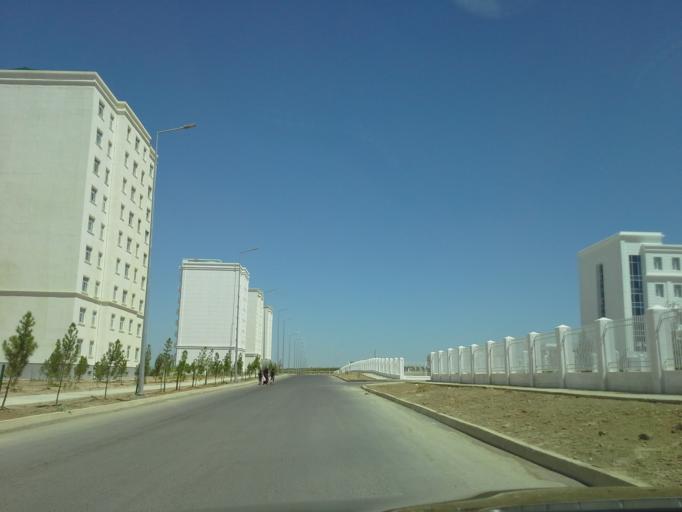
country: TM
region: Ahal
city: Ashgabat
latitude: 37.8884
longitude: 58.4079
